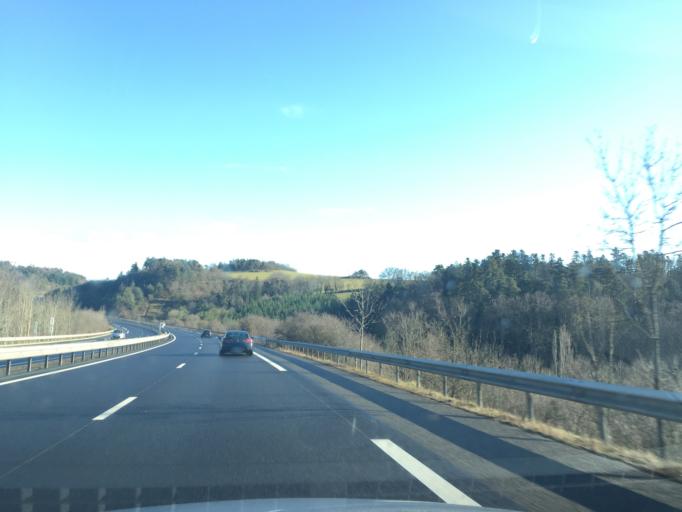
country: FR
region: Rhone-Alpes
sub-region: Departement de la Loire
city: Saint-Just-en-Chevalet
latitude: 45.8732
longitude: 3.9073
